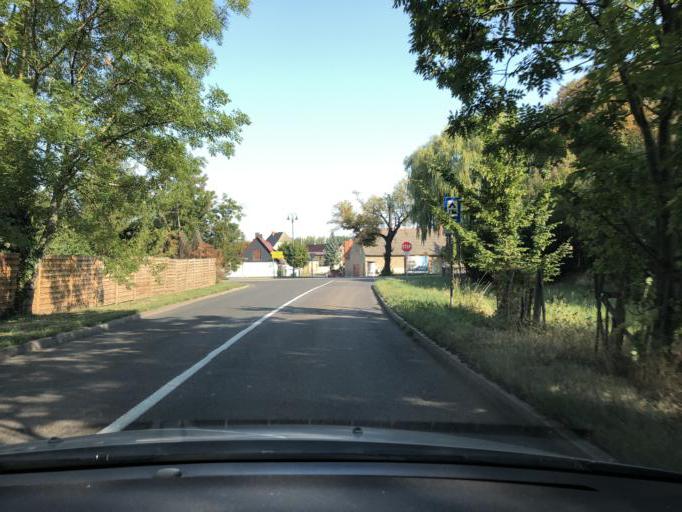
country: DE
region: Saxony-Anhalt
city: Braunsbedra
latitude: 51.2622
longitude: 11.8746
